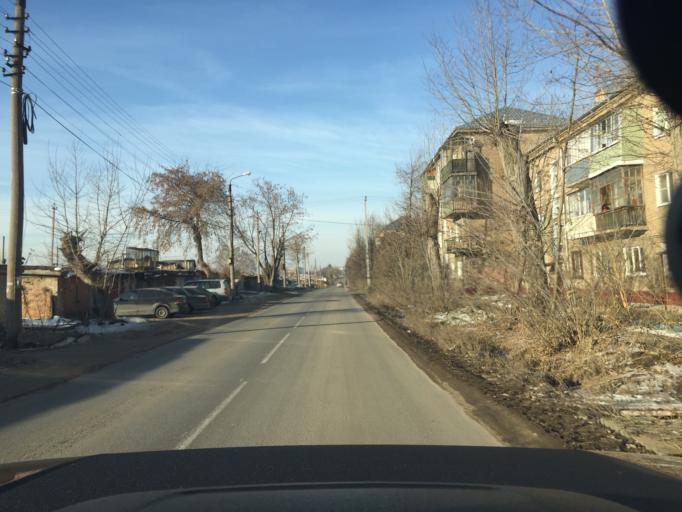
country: RU
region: Tula
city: Tula
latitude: 54.1795
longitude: 37.7011
